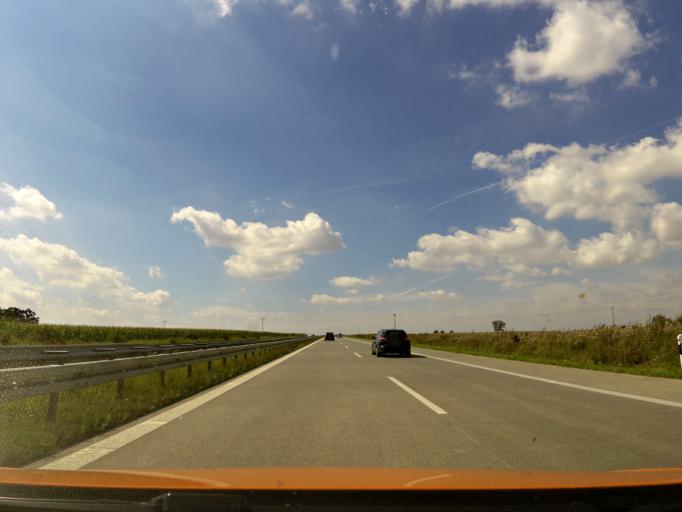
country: DE
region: Mecklenburg-Vorpommern
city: Penkun
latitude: 53.3117
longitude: 14.2491
